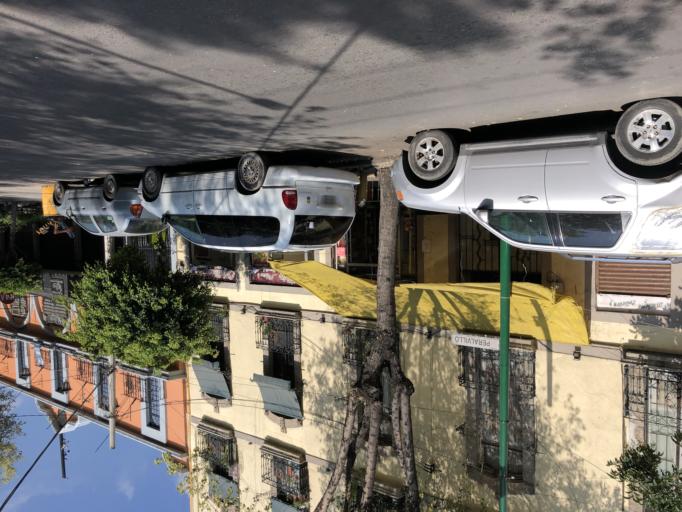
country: MX
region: Mexico City
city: Cuauhtemoc
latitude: 19.4442
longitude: -99.1327
